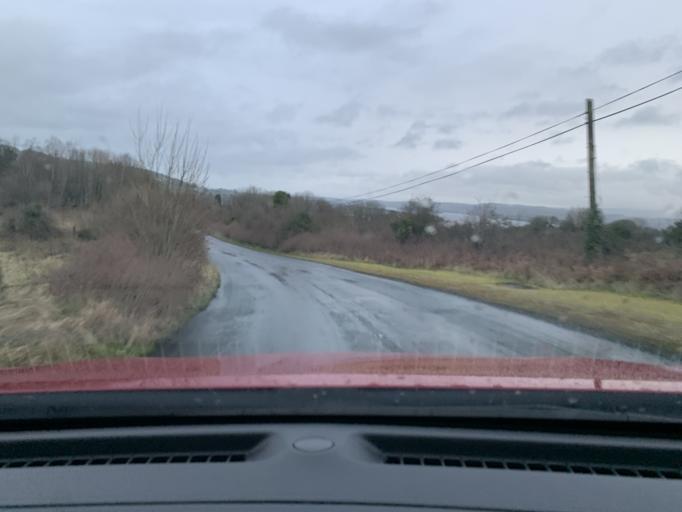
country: IE
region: Connaught
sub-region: Roscommon
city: Boyle
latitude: 54.0225
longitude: -8.3281
